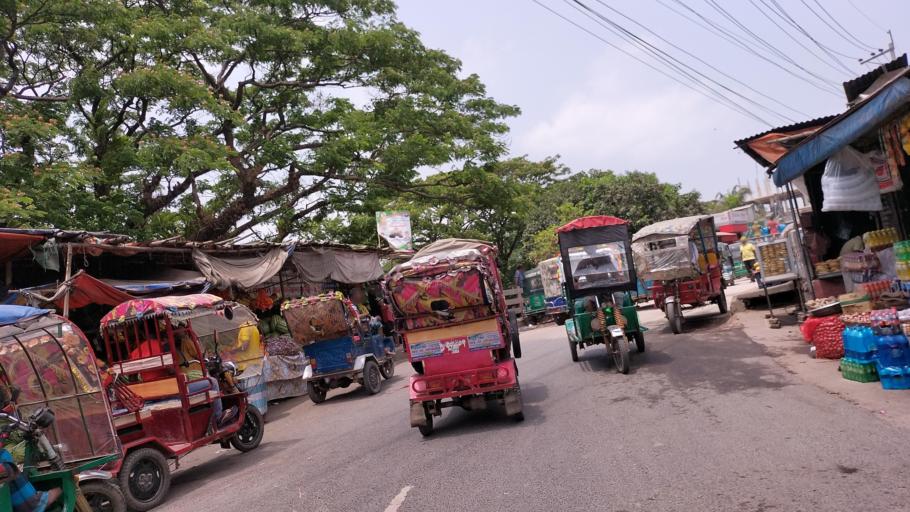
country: BD
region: Dhaka
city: Azimpur
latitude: 23.7319
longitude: 90.2734
